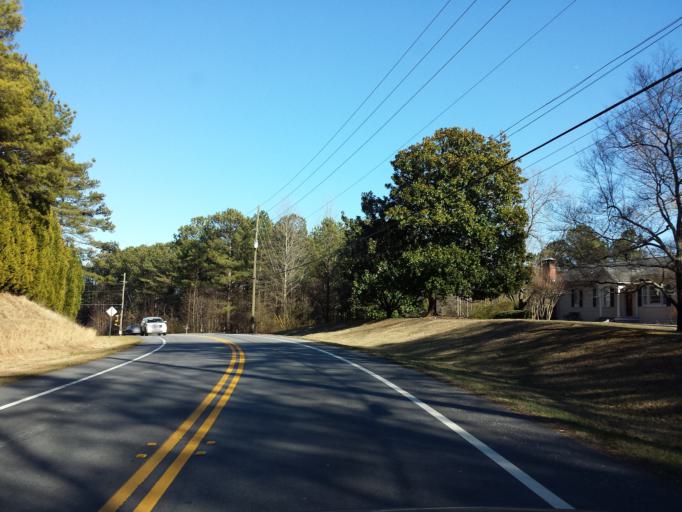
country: US
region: Georgia
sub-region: Cobb County
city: Kennesaw
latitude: 33.9649
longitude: -84.6558
